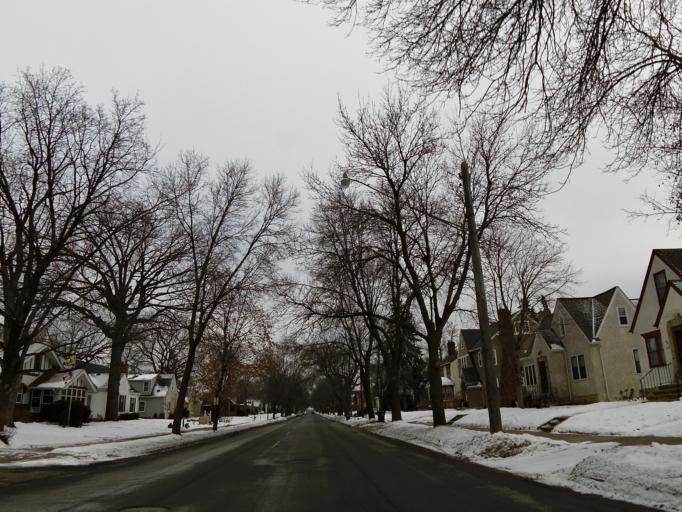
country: US
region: Minnesota
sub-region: Dakota County
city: Mendota Heights
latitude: 44.9263
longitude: -93.1925
